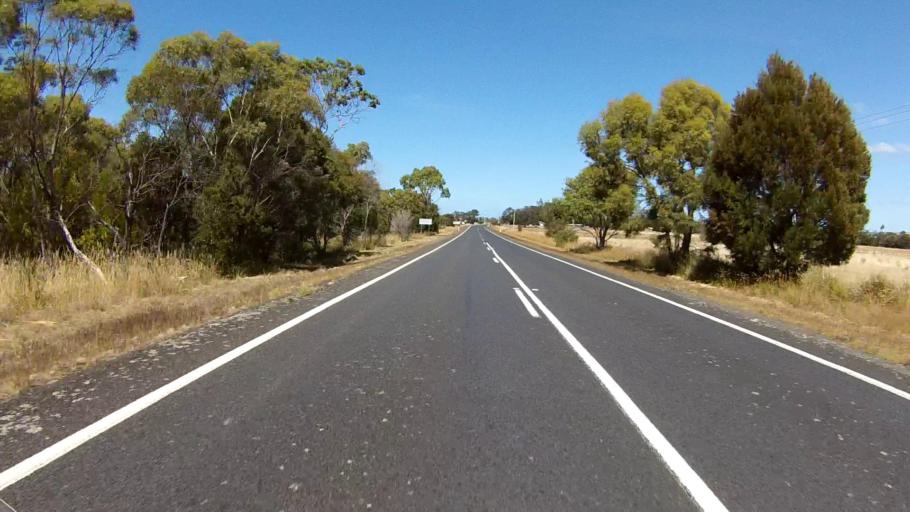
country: AU
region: Tasmania
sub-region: Break O'Day
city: St Helens
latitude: -42.0565
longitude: 148.0589
